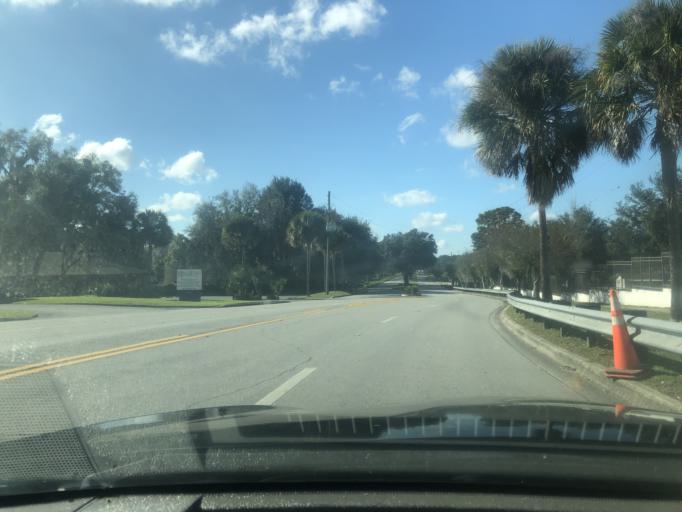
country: US
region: Florida
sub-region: Citrus County
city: Inverness
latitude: 28.8323
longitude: -82.3370
